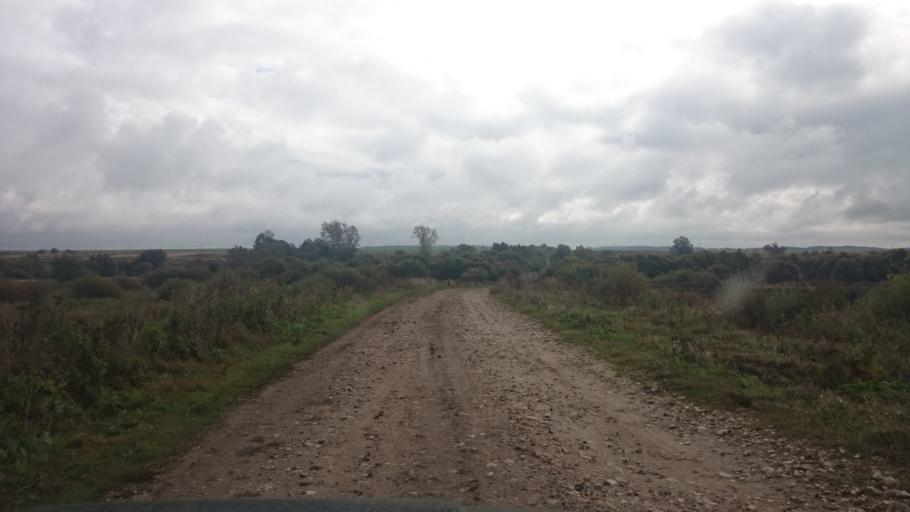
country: RU
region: Mordoviya
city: Kadoshkino
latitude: 54.0194
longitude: 44.4519
